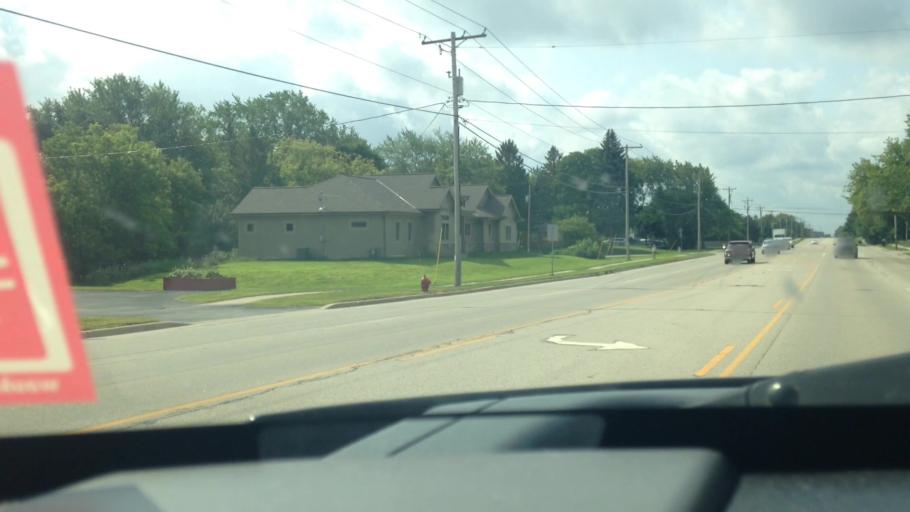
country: US
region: Wisconsin
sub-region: Waukesha County
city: Menomonee Falls
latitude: 43.1560
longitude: -88.1043
